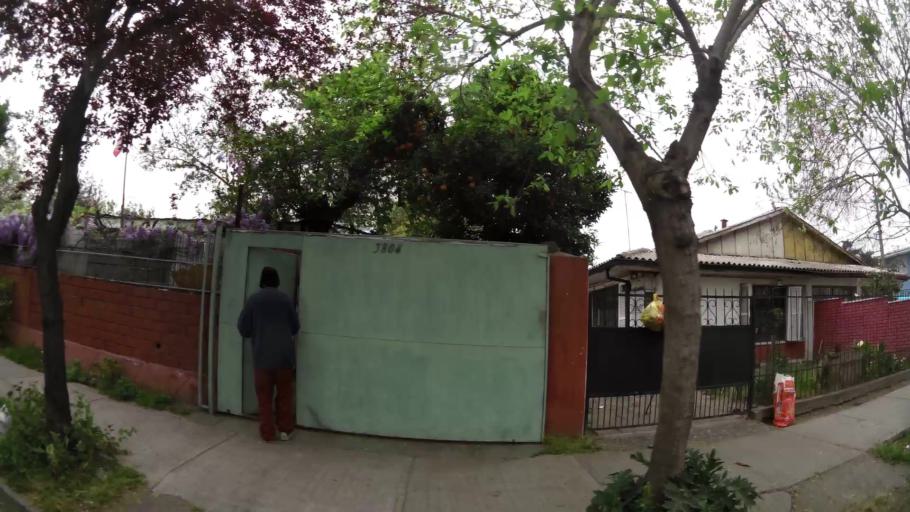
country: CL
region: Santiago Metropolitan
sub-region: Provincia de Santiago
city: Villa Presidente Frei, Nunoa, Santiago, Chile
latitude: -33.4889
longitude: -70.6017
